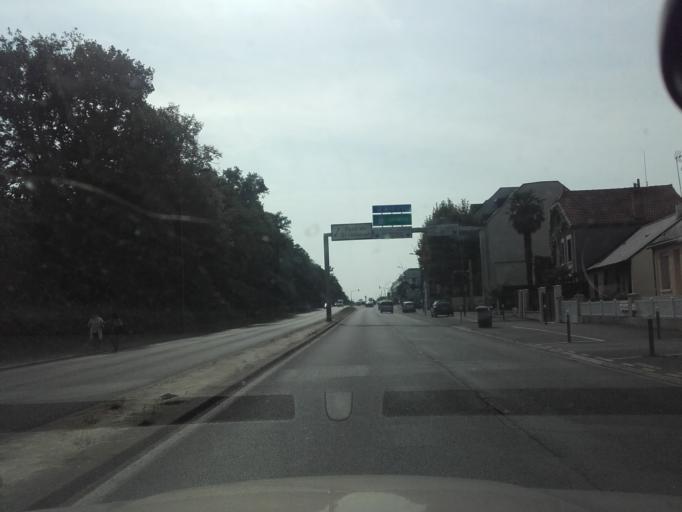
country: FR
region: Centre
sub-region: Departement d'Indre-et-Loire
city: Chambray-les-Tours
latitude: 47.3580
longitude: 0.6981
